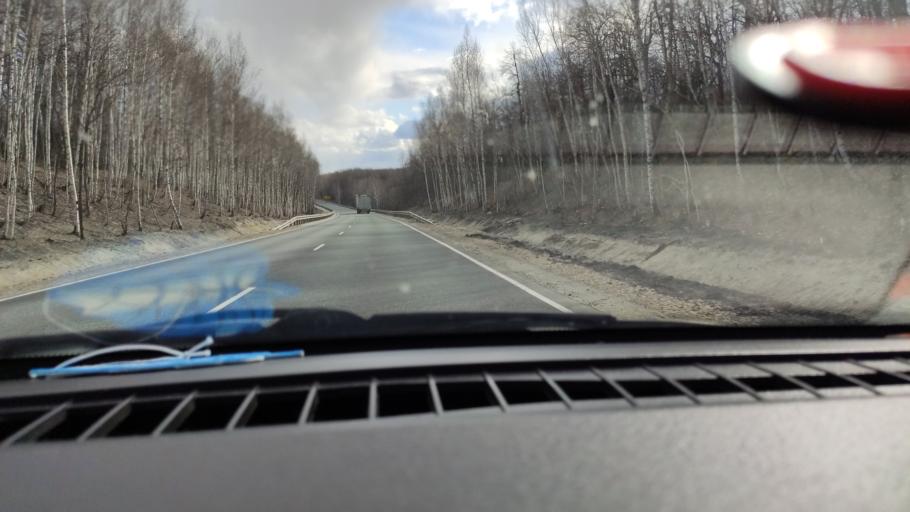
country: RU
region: Saratov
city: Khvalynsk
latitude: 52.4416
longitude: 48.0096
